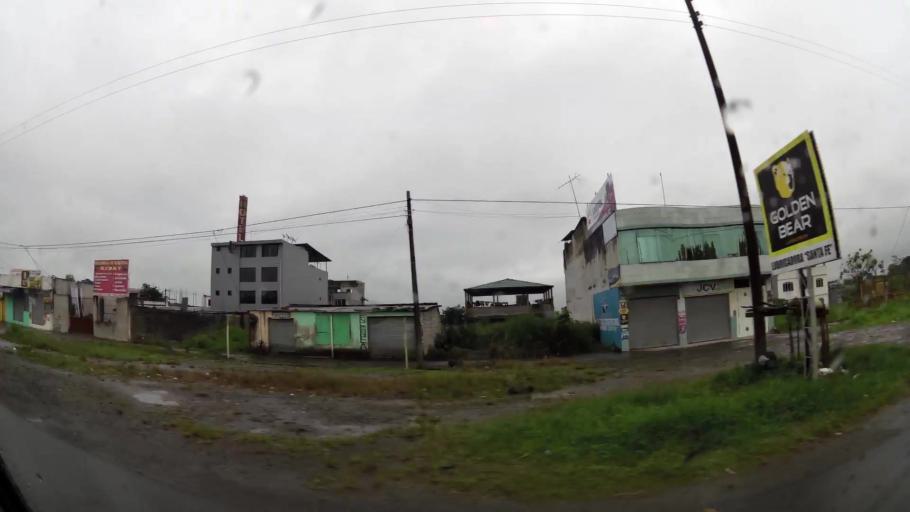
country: EC
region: Santo Domingo de los Tsachilas
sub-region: Canton Santo Domingo de los Colorados
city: Santo Domingo de los Colorados
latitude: -0.2319
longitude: -79.1628
